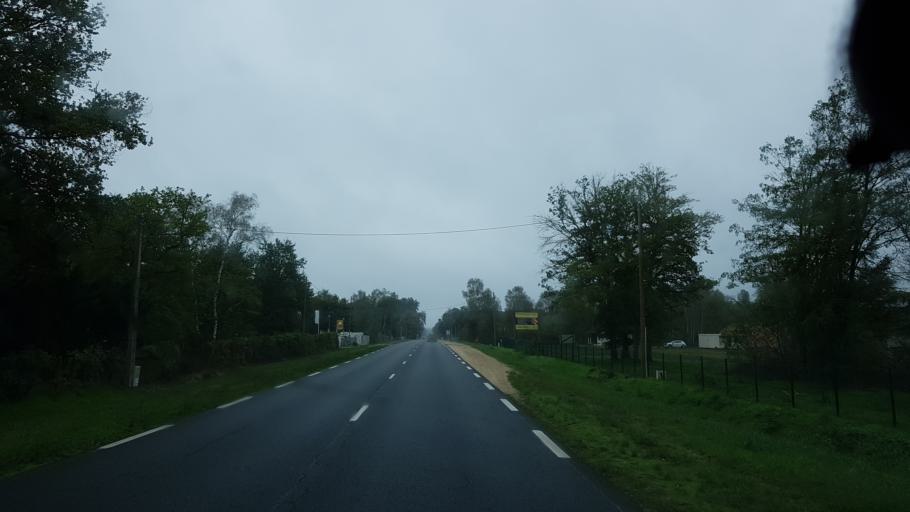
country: FR
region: Centre
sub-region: Departement du Loir-et-Cher
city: Salbris
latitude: 47.4413
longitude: 2.0469
